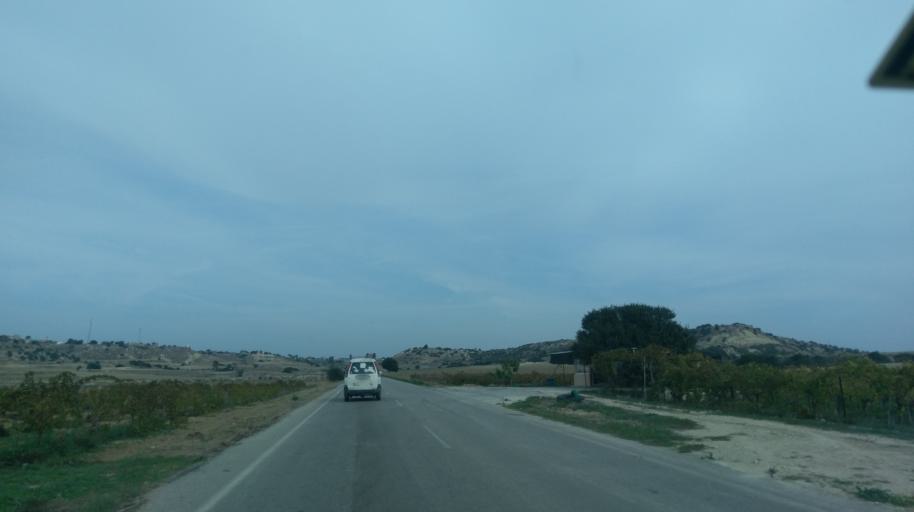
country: CY
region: Ammochostos
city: Leonarisso
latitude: 35.4585
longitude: 34.1314
